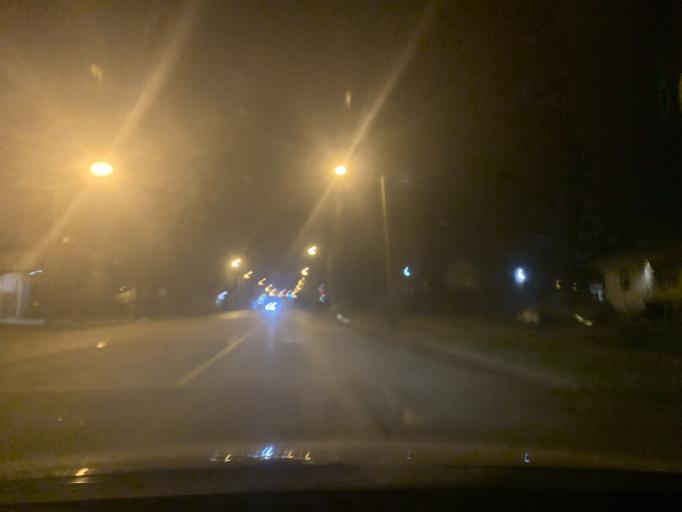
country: US
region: Indiana
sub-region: Saint Joseph County
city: South Bend
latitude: 41.6498
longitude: -86.2497
